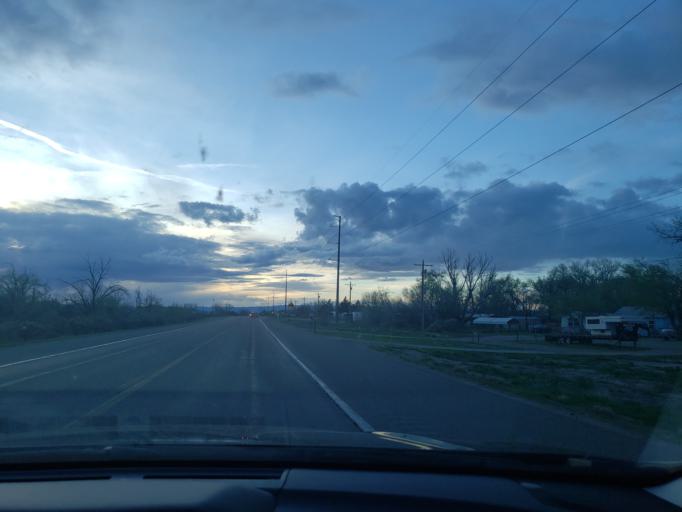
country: US
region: Colorado
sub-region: Mesa County
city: Fruita
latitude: 39.1276
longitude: -108.6789
